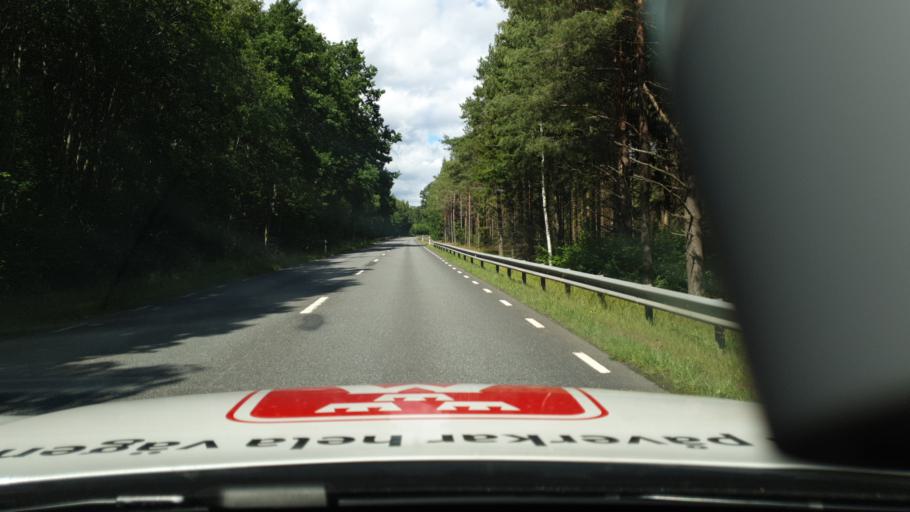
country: SE
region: Vaestra Goetaland
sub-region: Hjo Kommun
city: Hjo
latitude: 58.1078
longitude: 14.2083
